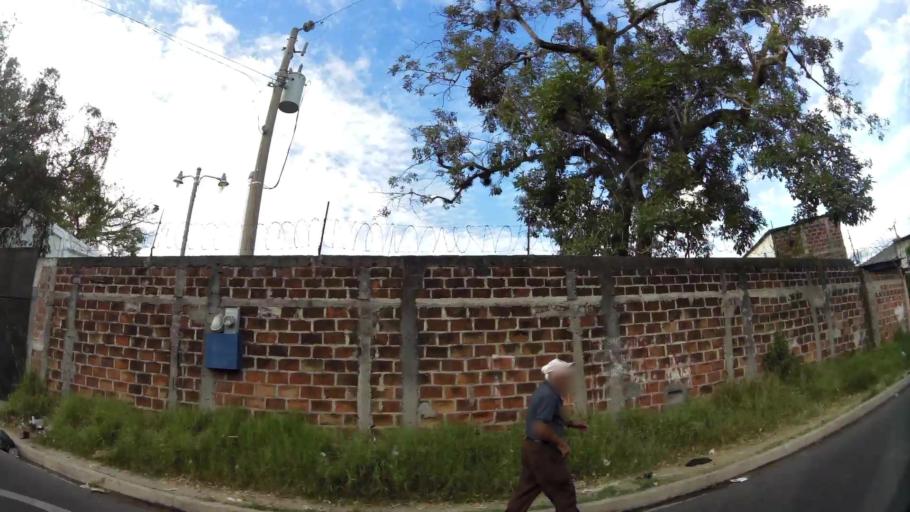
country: SV
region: Cuscatlan
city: Cojutepeque
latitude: 13.7214
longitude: -88.9288
